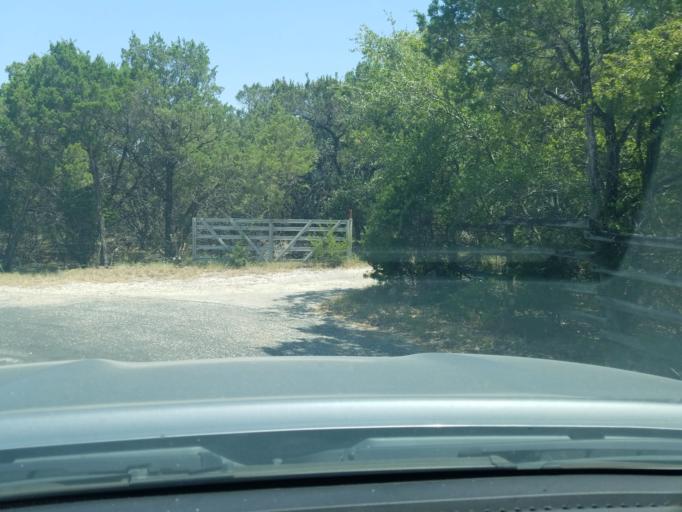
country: US
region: Texas
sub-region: Bexar County
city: Timberwood Park
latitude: 29.7216
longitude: -98.4922
